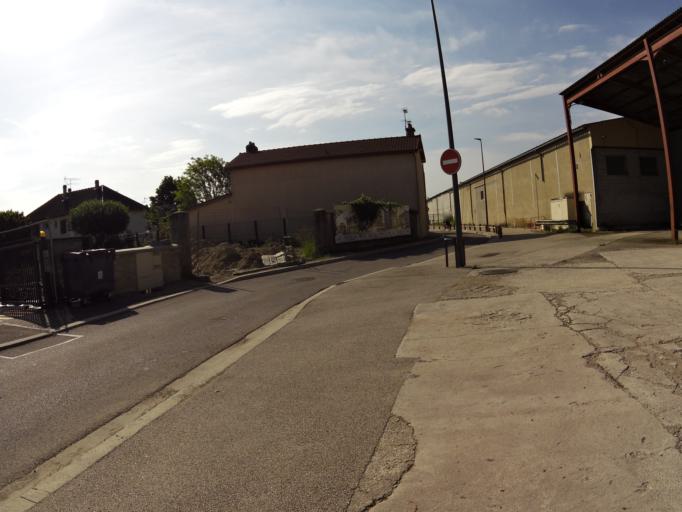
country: FR
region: Champagne-Ardenne
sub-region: Departement de l'Aube
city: Saint-Julien-les-Villas
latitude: 48.2850
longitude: 4.0905
